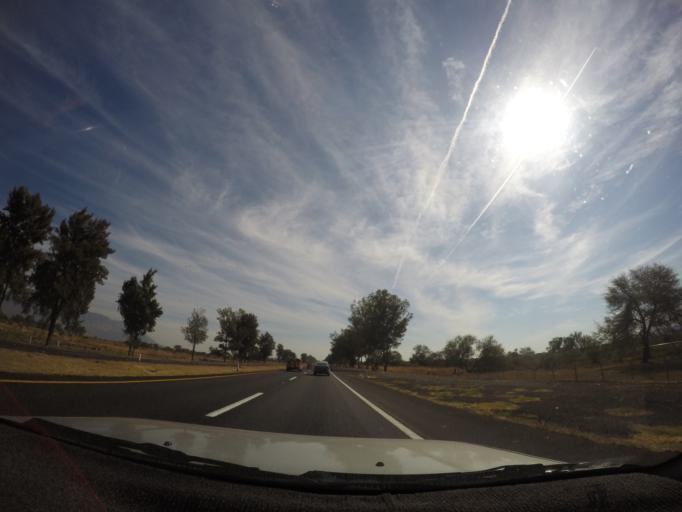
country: MX
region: Jalisco
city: Jamay
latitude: 20.3508
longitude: -102.6336
